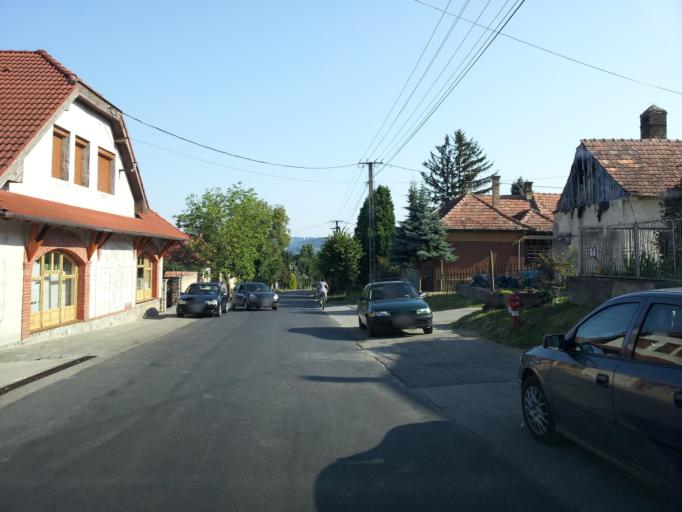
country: HU
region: Zala
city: Gyenesdias
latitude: 46.8631
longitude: 17.2979
